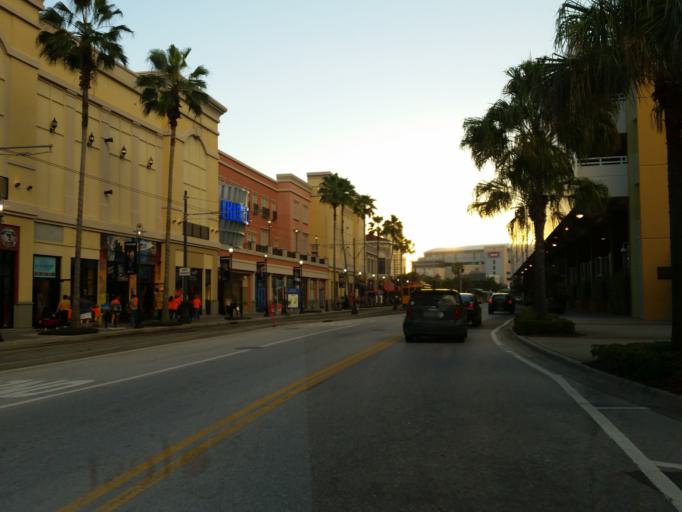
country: US
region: Florida
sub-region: Hillsborough County
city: Tampa
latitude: 27.9441
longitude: -82.4462
